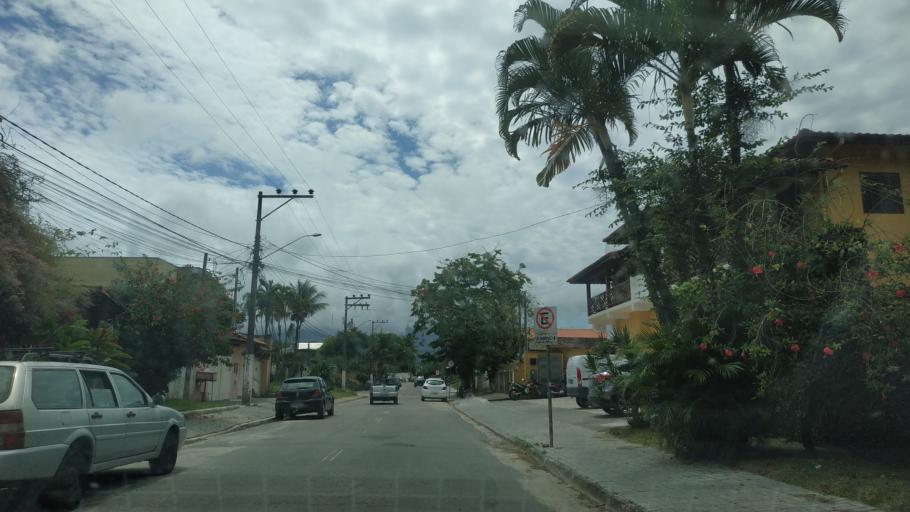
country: BR
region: Sao Paulo
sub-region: Ilhabela
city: Ilhabela
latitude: -23.8215
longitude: -45.3682
